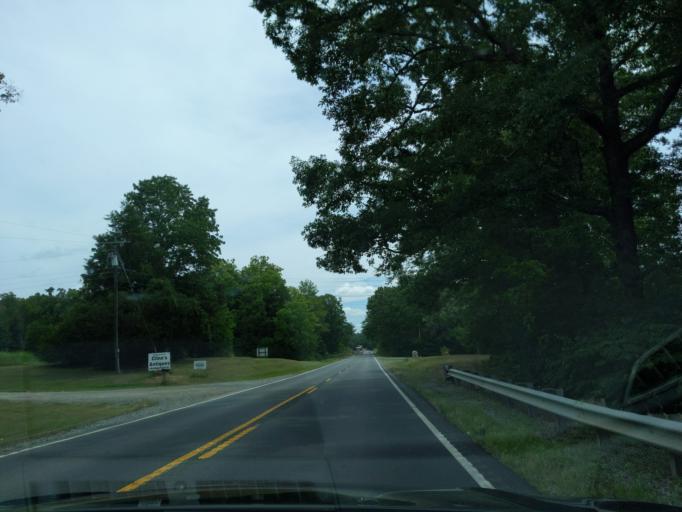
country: US
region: North Carolina
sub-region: Cabarrus County
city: Mount Pleasant
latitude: 35.4382
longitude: -80.3767
